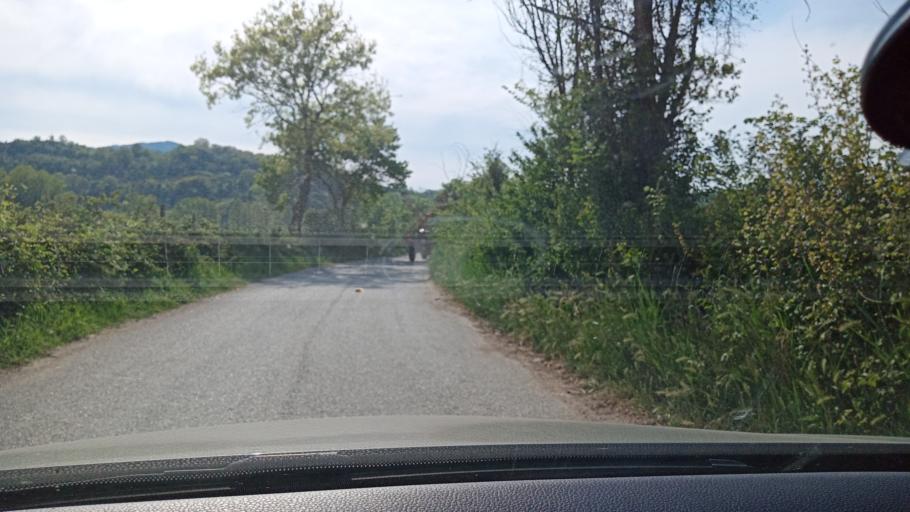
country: IT
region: Latium
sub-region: Citta metropolitana di Roma Capitale
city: Ponzano Romano
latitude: 42.2674
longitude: 12.5580
